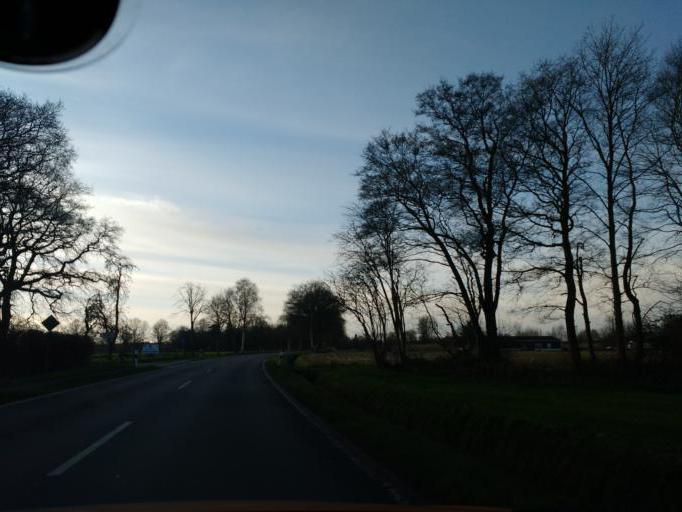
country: DE
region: Lower Saxony
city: Hude
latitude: 53.1082
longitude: 8.4366
